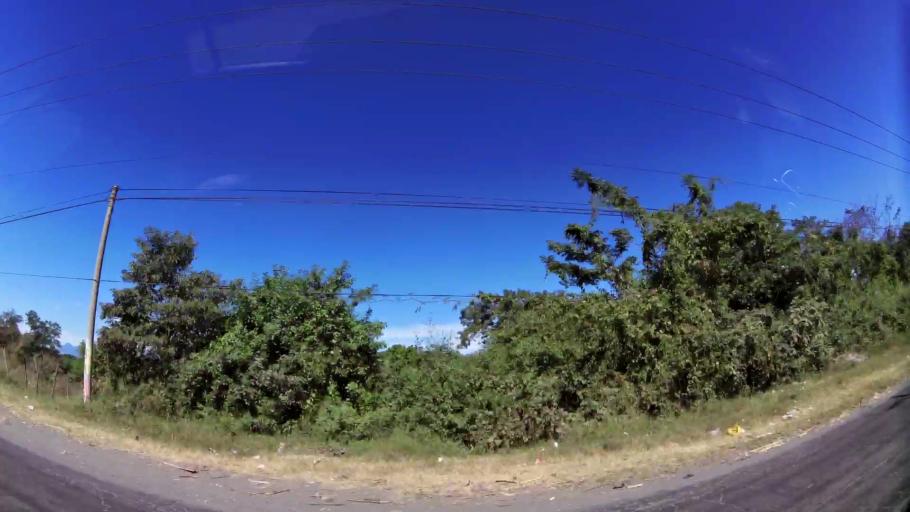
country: SV
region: La Libertad
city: San Juan Opico
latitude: 13.8023
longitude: -89.3600
